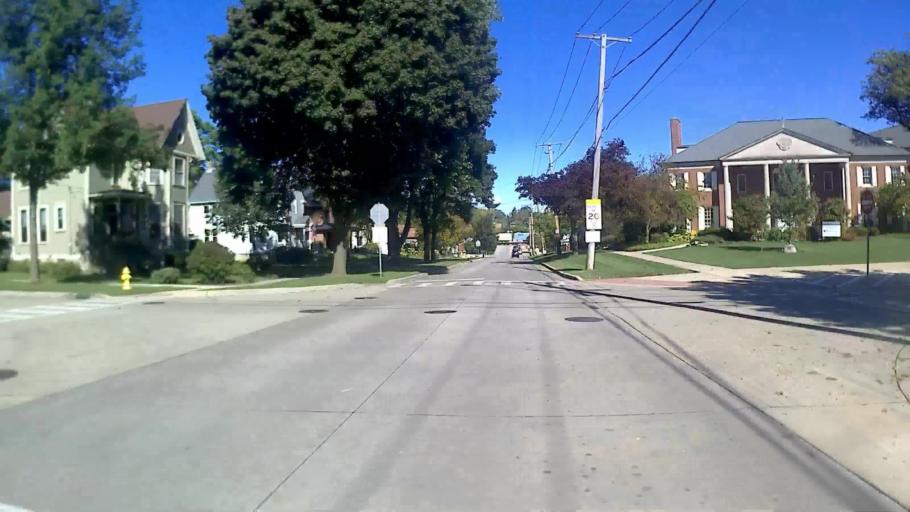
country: US
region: Illinois
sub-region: DuPage County
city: Glen Ellyn
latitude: 41.8738
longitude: -88.0701
